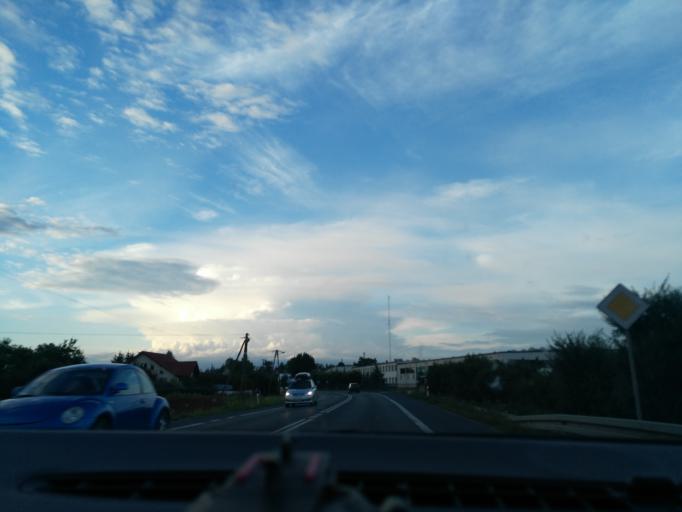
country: PL
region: Lublin Voivodeship
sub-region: Powiat lubelski
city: Niemce
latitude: 51.3629
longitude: 22.6297
